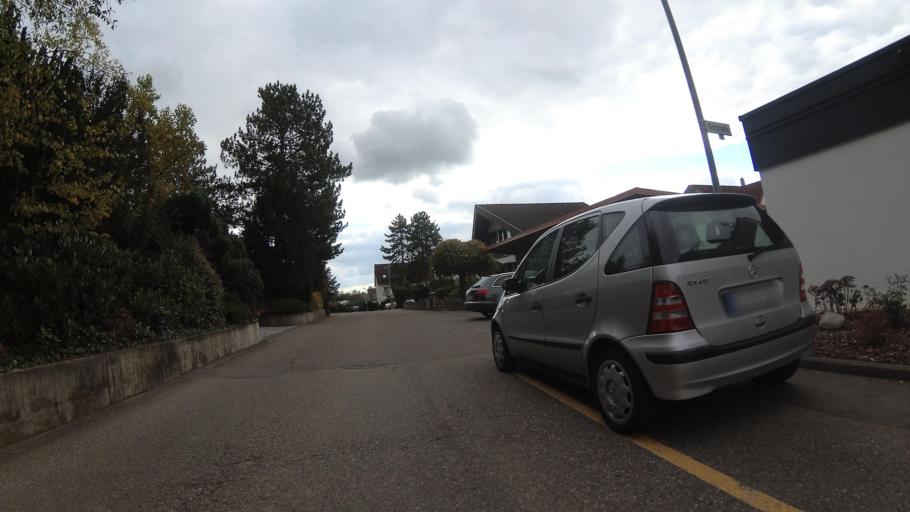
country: DE
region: Baden-Wuerttemberg
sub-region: Regierungsbezirk Stuttgart
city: Untereisesheim
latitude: 49.2253
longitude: 9.2267
